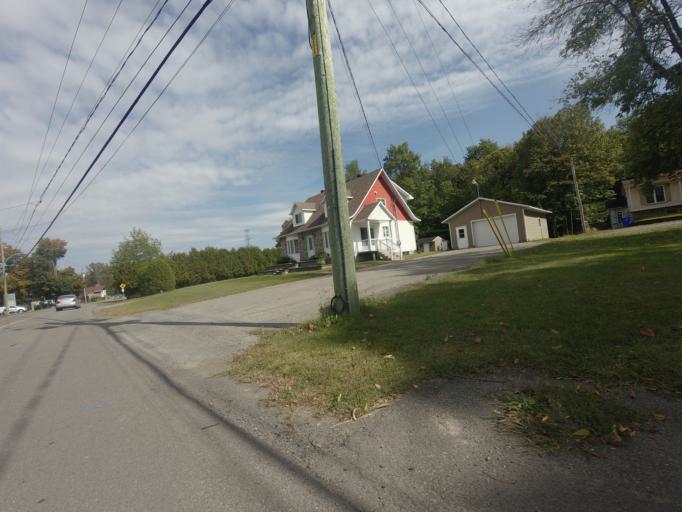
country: CA
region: Quebec
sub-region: Laurentides
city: Blainville
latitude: 45.6243
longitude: -73.9113
